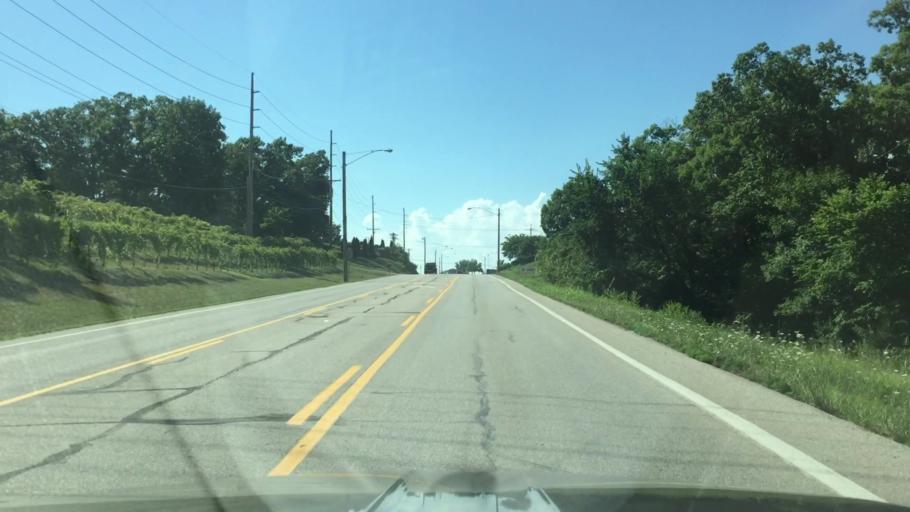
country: US
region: Missouri
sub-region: Miller County
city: Lake Ozark
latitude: 38.1844
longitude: -92.6365
